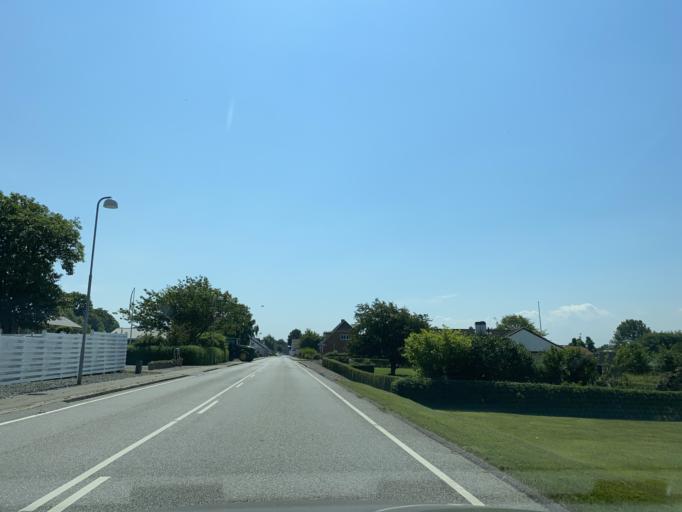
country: DK
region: South Denmark
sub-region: Sonderborg Kommune
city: Grasten
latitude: 54.9992
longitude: 9.5810
